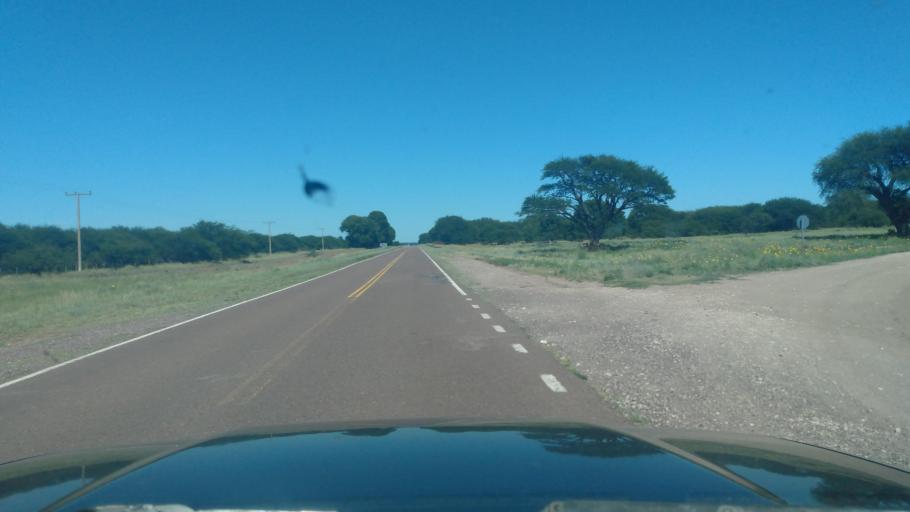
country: AR
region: La Pampa
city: General Acha
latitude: -37.4175
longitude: -64.8537
